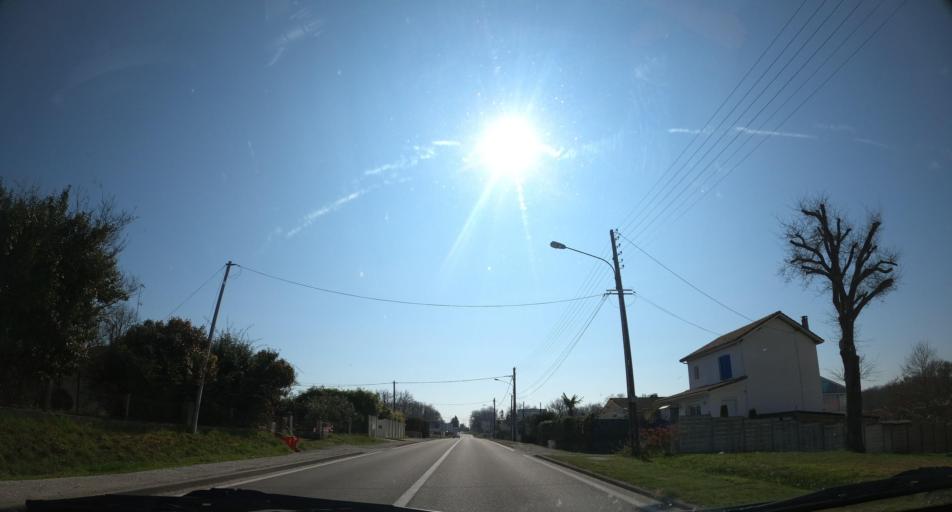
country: FR
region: Aquitaine
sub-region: Departement des Landes
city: Mont-de-Marsan
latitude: 43.8647
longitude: -0.4870
